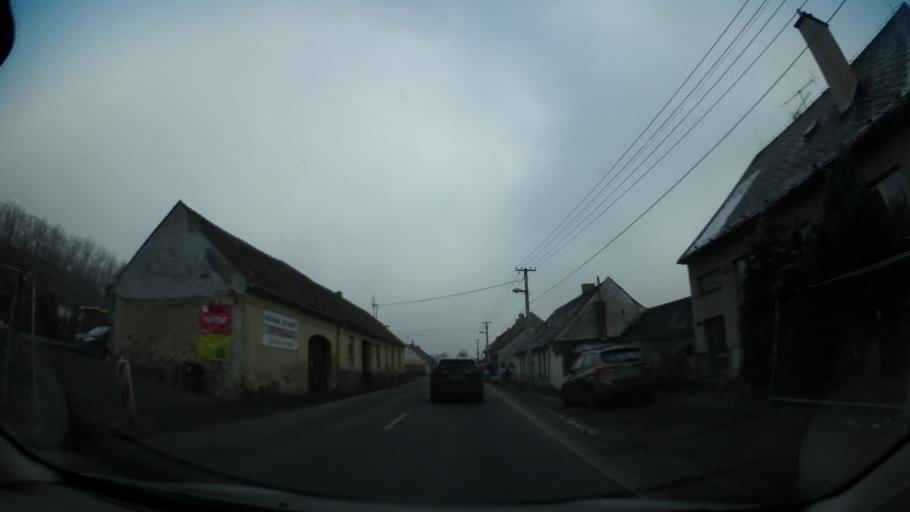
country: CZ
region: Vysocina
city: Vladislav
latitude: 49.2114
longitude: 15.9808
